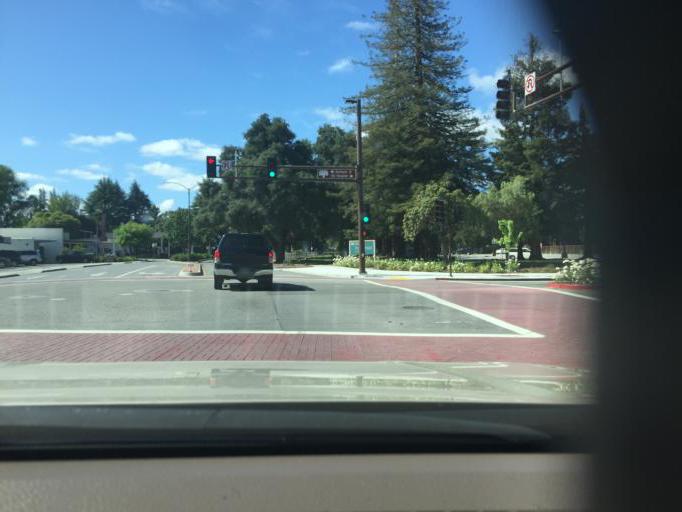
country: US
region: California
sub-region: San Mateo County
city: East Palo Alto
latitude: 37.4653
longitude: -122.1574
